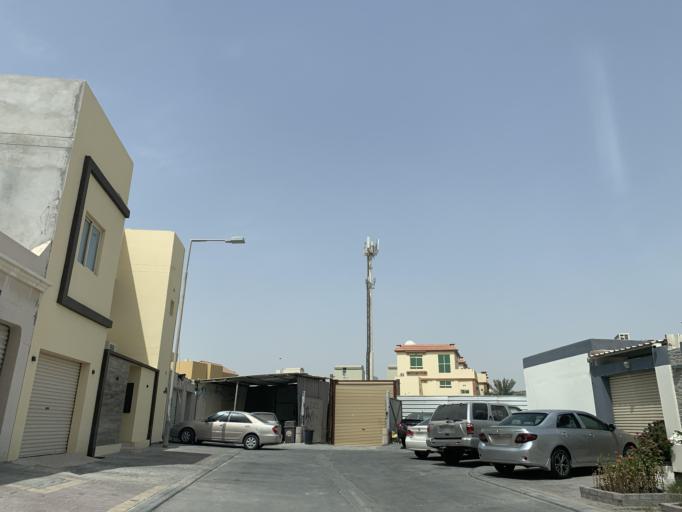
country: BH
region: Northern
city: Madinat `Isa
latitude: 26.1725
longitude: 50.5242
